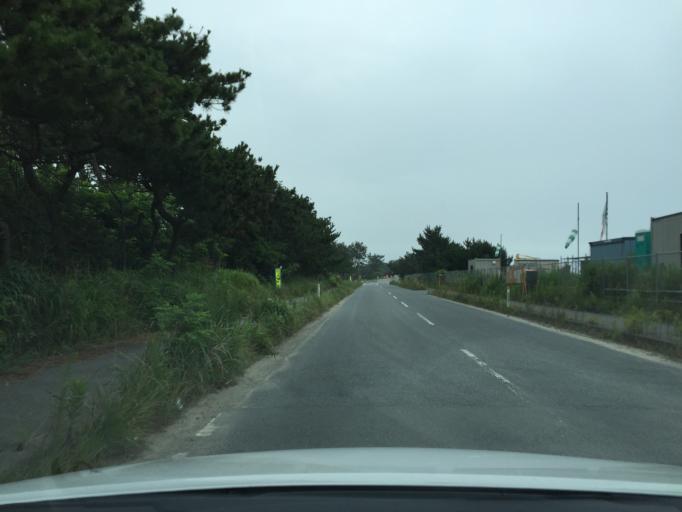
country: JP
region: Fukushima
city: Iwaki
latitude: 37.0207
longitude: 140.9713
